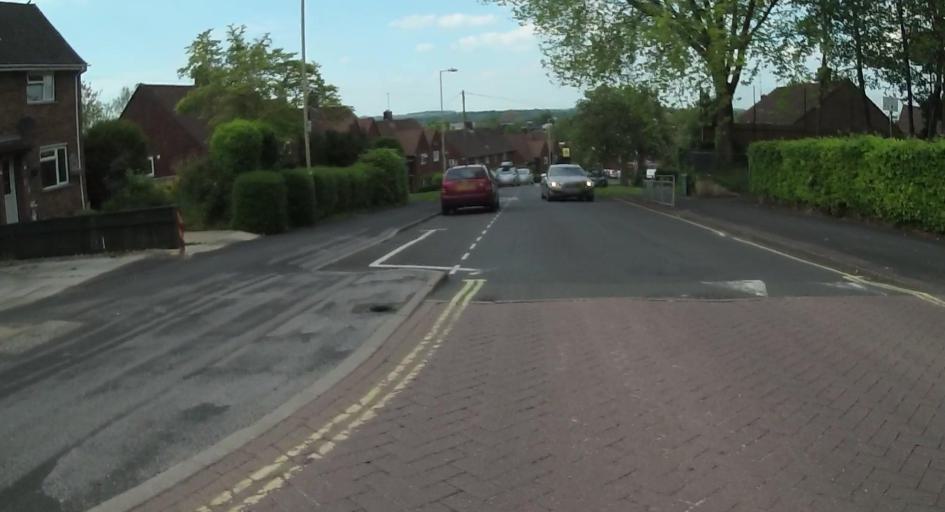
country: GB
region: England
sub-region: Hampshire
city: Winchester
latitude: 51.0633
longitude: -1.2991
